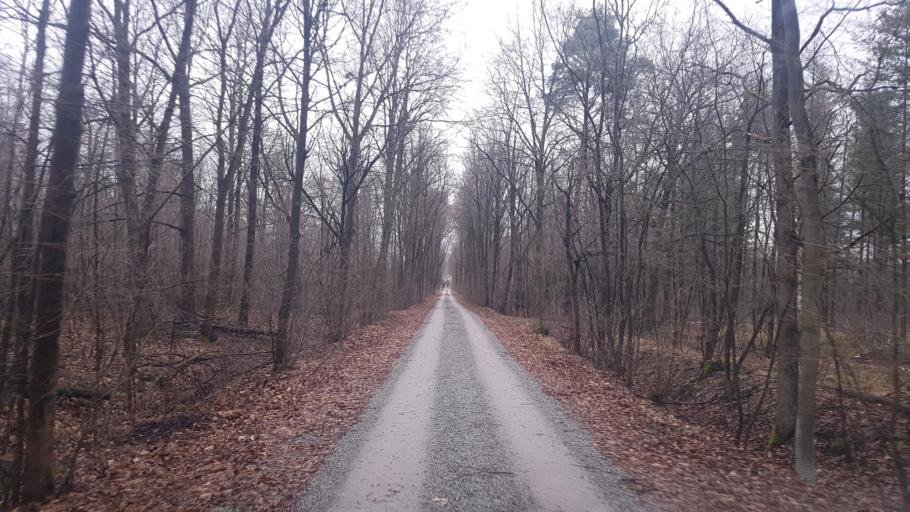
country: DE
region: Brandenburg
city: Plessa
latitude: 51.4430
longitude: 13.6511
